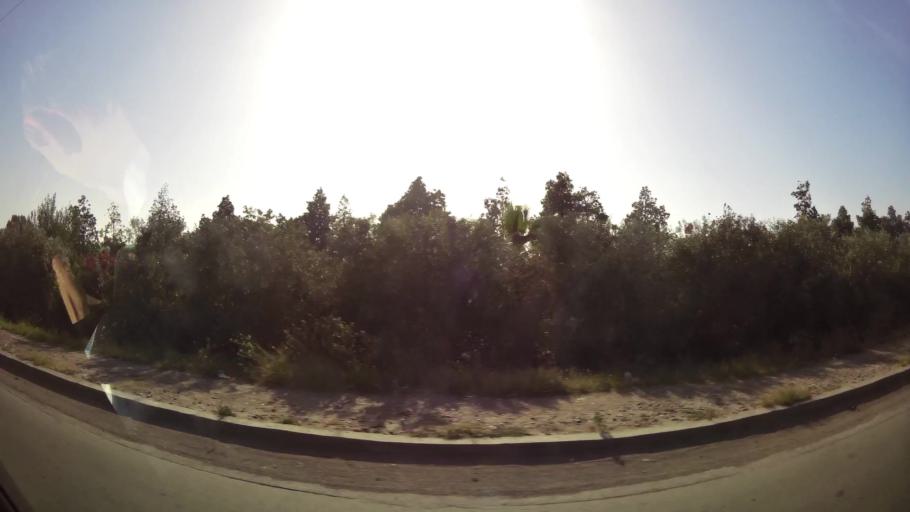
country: MA
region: Souss-Massa-Draa
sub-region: Inezgane-Ait Mellou
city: Inezgane
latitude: 30.3622
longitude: -9.5060
